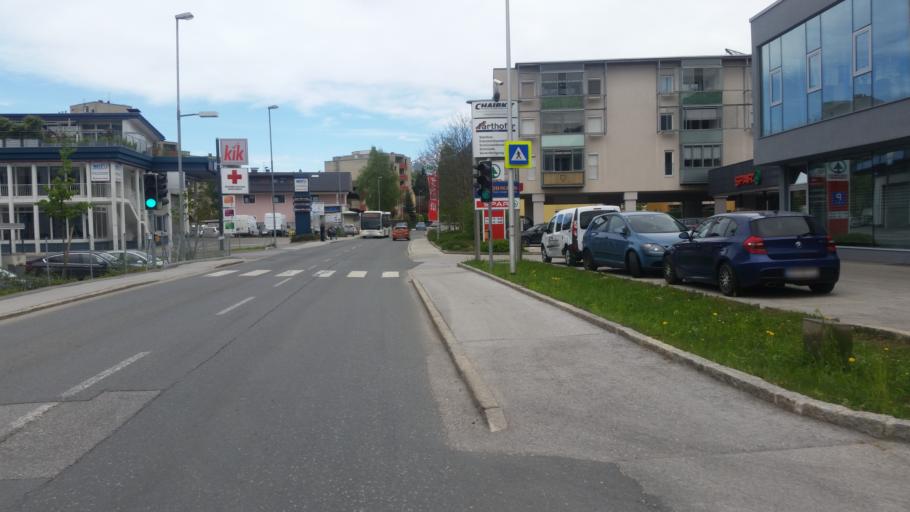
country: AT
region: Tyrol
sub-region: Politischer Bezirk Kufstein
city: Worgl
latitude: 47.4870
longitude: 12.0761
